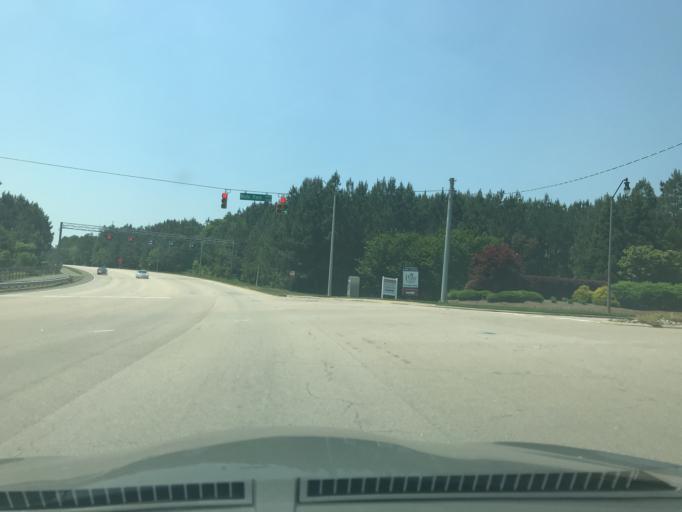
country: US
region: North Carolina
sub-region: Wake County
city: Cary
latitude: 35.8048
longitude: -78.7261
